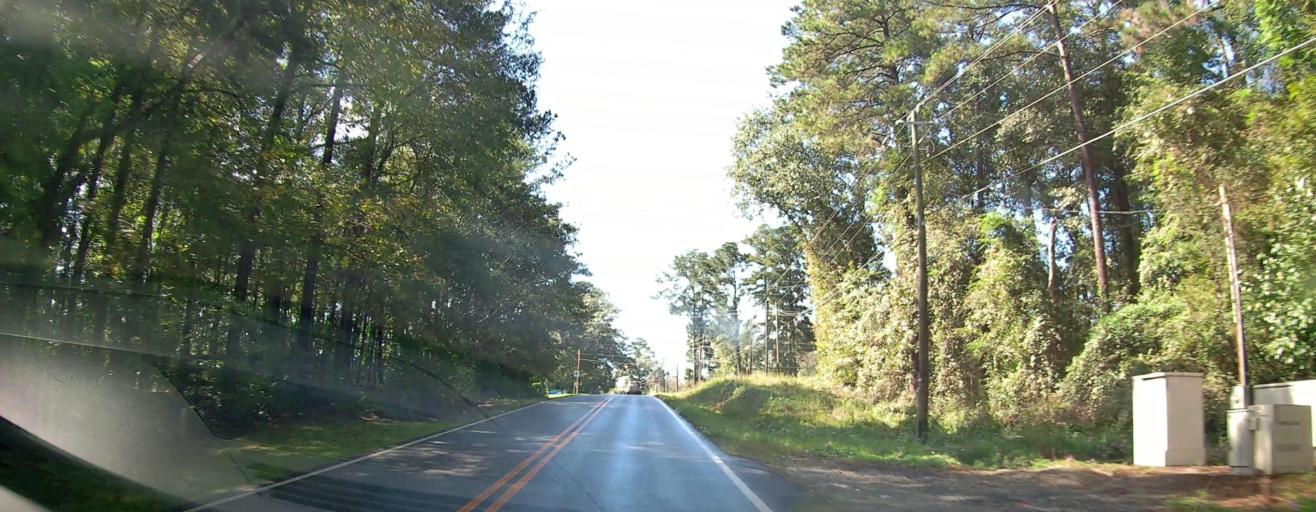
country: US
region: Georgia
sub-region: Bibb County
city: Macon
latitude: 32.9192
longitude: -83.7192
